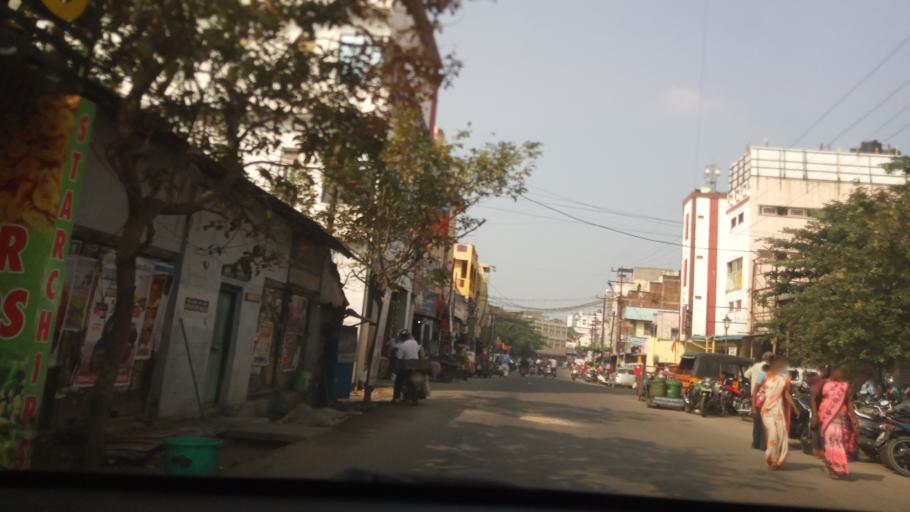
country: IN
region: Tamil Nadu
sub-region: Coimbatore
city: Coimbatore
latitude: 10.9997
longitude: 76.9524
